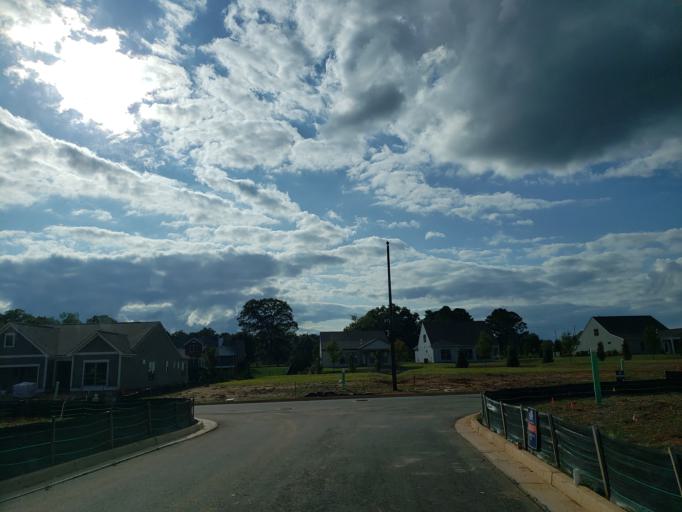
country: US
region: Georgia
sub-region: Cobb County
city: Powder Springs
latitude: 33.8870
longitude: -84.6826
